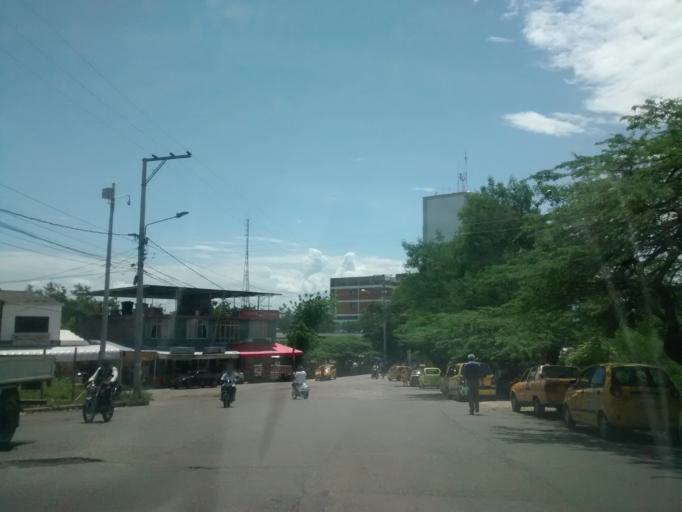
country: CO
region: Cundinamarca
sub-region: Girardot
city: Girardot City
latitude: 4.2964
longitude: -74.7987
